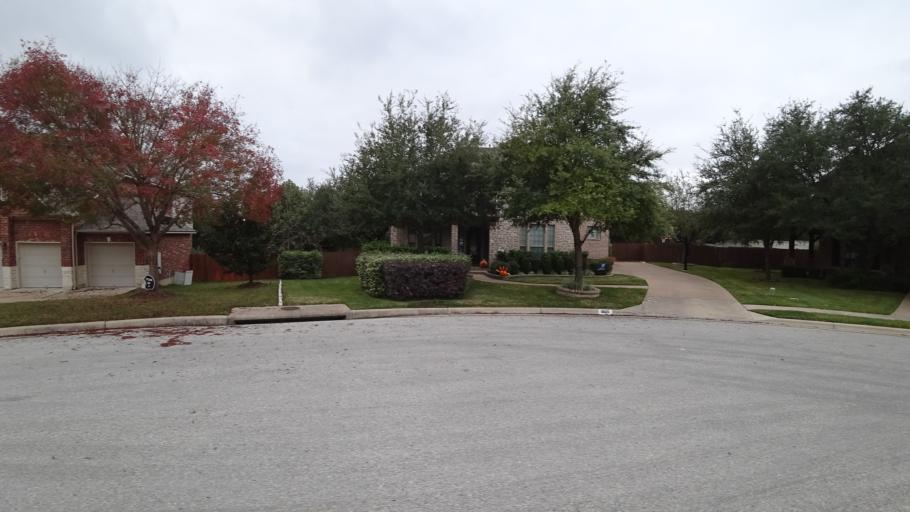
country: US
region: Texas
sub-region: Travis County
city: Hudson Bend
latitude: 30.3582
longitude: -97.9043
